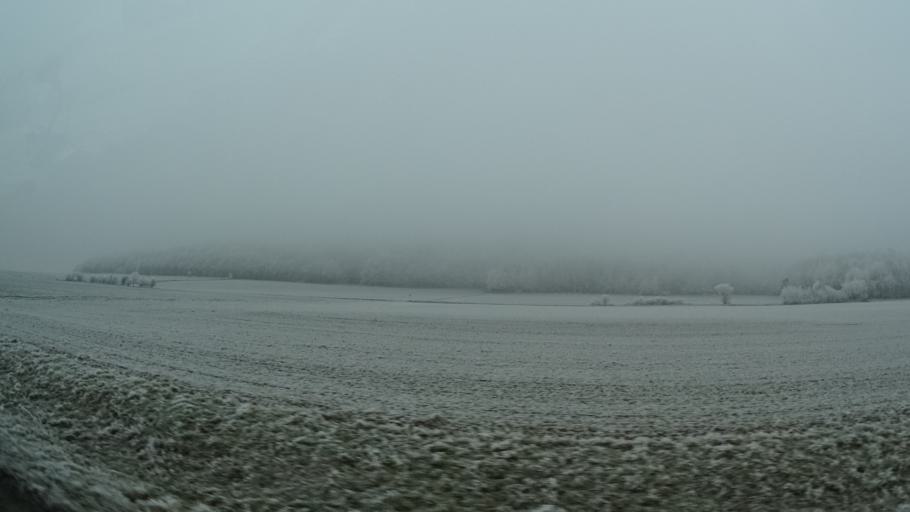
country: DE
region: Bavaria
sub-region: Regierungsbezirk Unterfranken
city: Willmars
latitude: 50.5072
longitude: 10.2519
